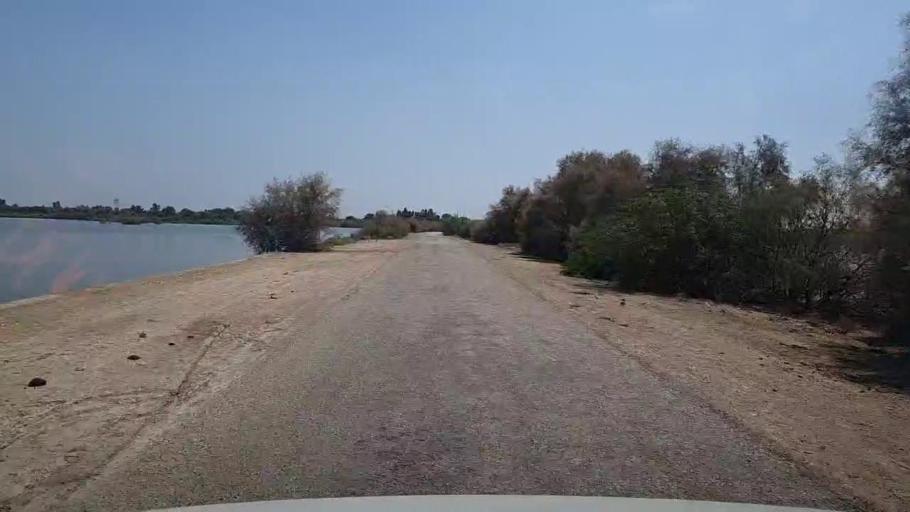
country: PK
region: Sindh
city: Kandhkot
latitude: 28.2971
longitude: 69.3520
